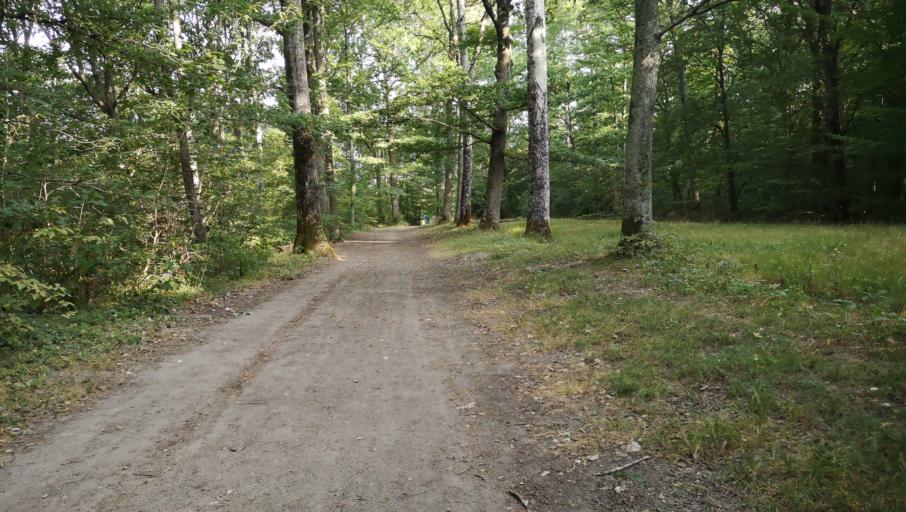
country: FR
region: Centre
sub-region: Departement du Loiret
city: Boigny-sur-Bionne
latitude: 47.9376
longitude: 1.9973
